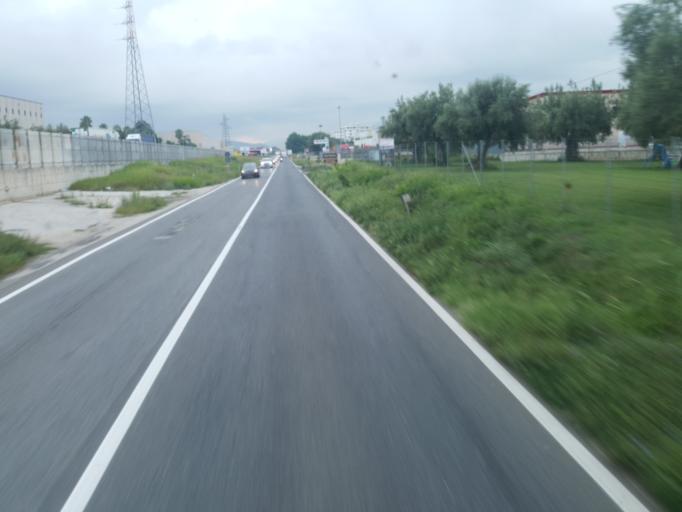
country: IT
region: Campania
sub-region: Provincia di Caserta
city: Pignataro Maggiore
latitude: 41.1662
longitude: 14.1582
